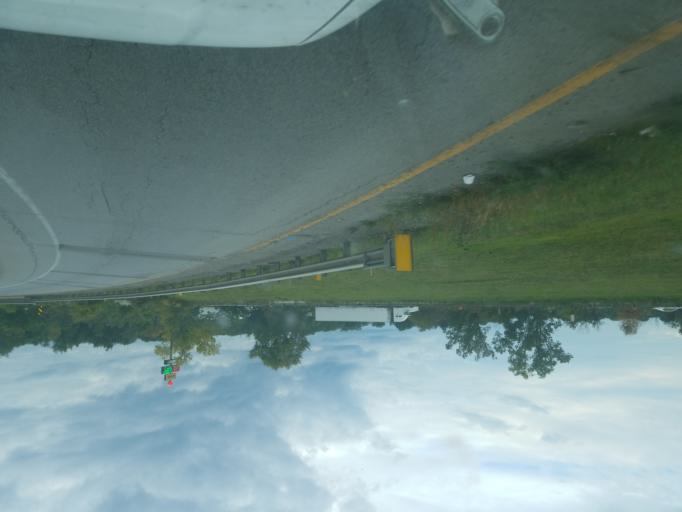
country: US
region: Ohio
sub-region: Trumbull County
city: Hubbard
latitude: 41.1768
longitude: -80.5712
